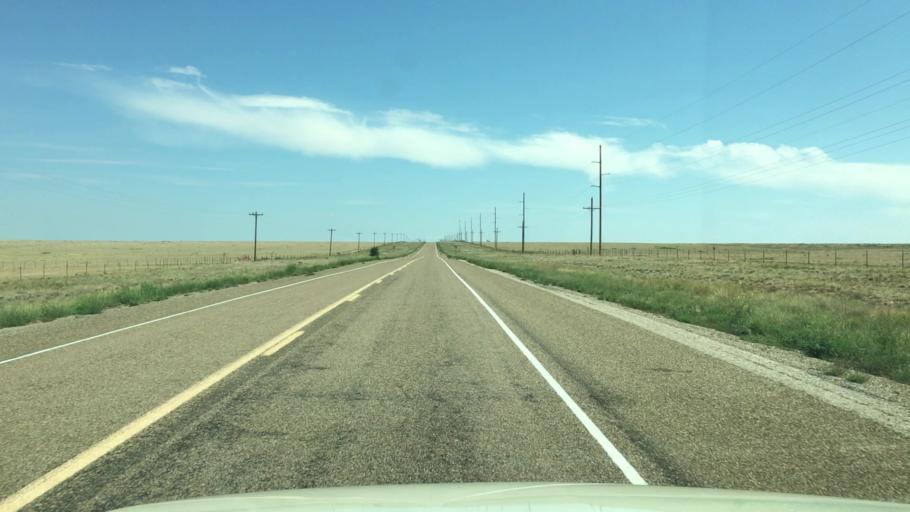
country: US
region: New Mexico
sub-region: Chaves County
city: Roswell
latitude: 33.9381
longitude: -104.5938
